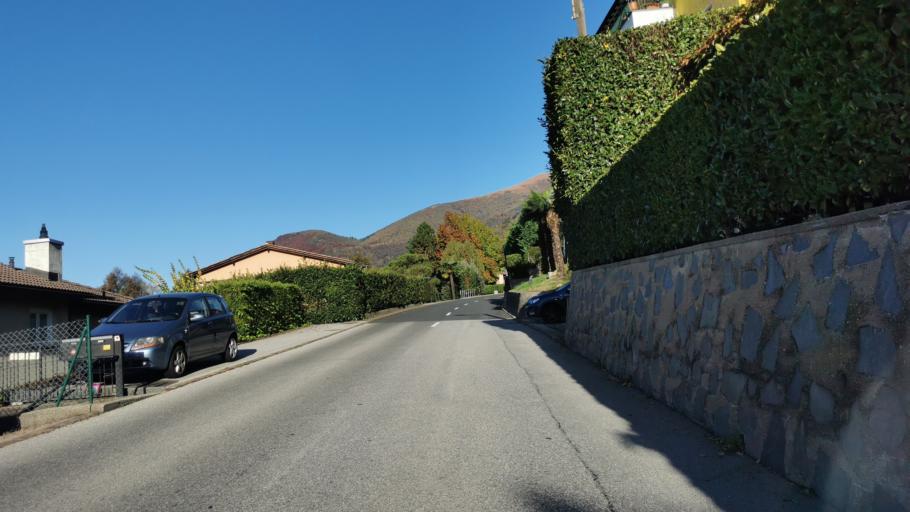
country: CH
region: Ticino
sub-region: Lugano District
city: Pura
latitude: 46.0031
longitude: 8.8599
